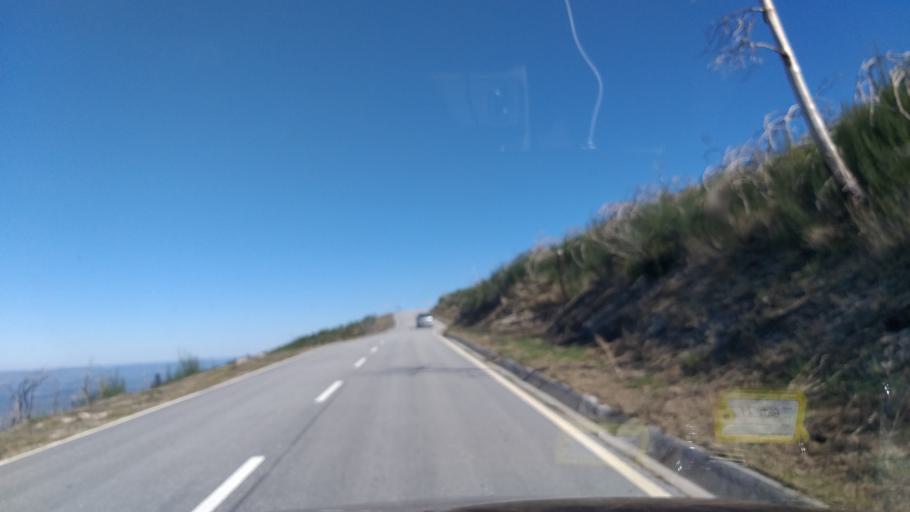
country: PT
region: Guarda
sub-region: Manteigas
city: Manteigas
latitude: 40.4929
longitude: -7.5477
